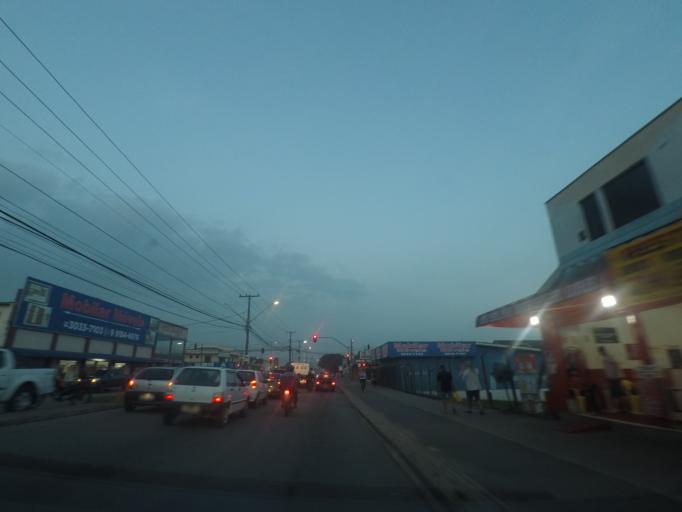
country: BR
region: Parana
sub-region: Pinhais
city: Pinhais
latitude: -25.4519
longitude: -49.1772
